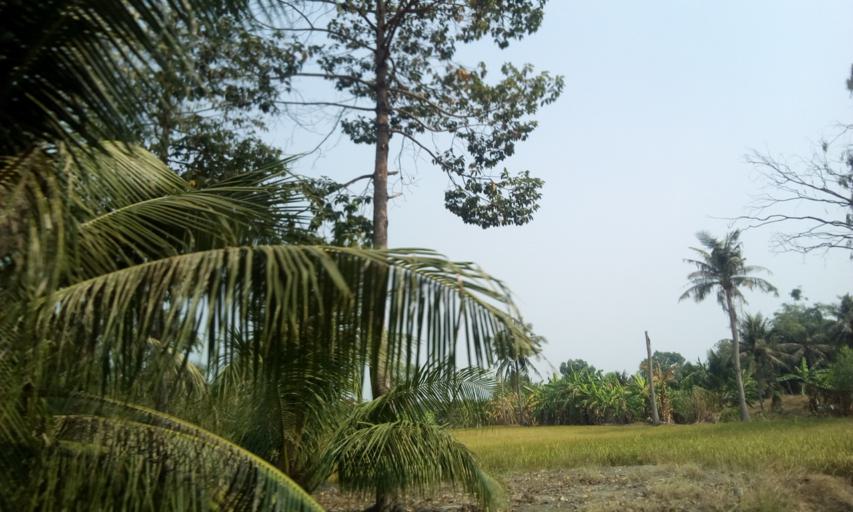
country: TH
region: Pathum Thani
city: Lam Luk Ka
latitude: 13.9432
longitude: 100.7243
